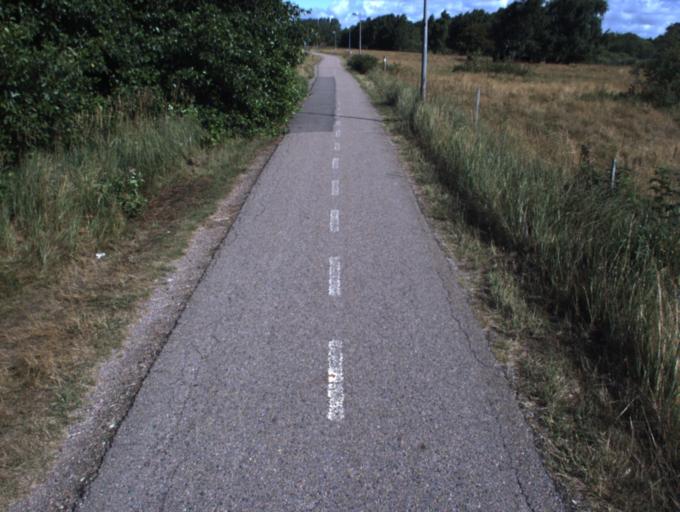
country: SE
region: Skane
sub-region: Helsingborg
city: Rydeback
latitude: 55.9845
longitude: 12.7538
